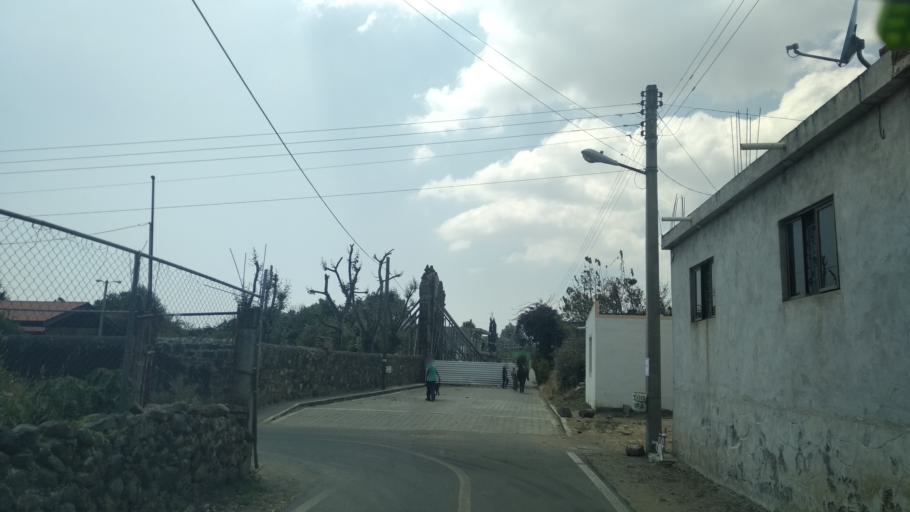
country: MX
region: Puebla
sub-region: Tochimilco
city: La Magdalena Yancuitlalpan
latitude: 18.8683
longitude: -98.6123
